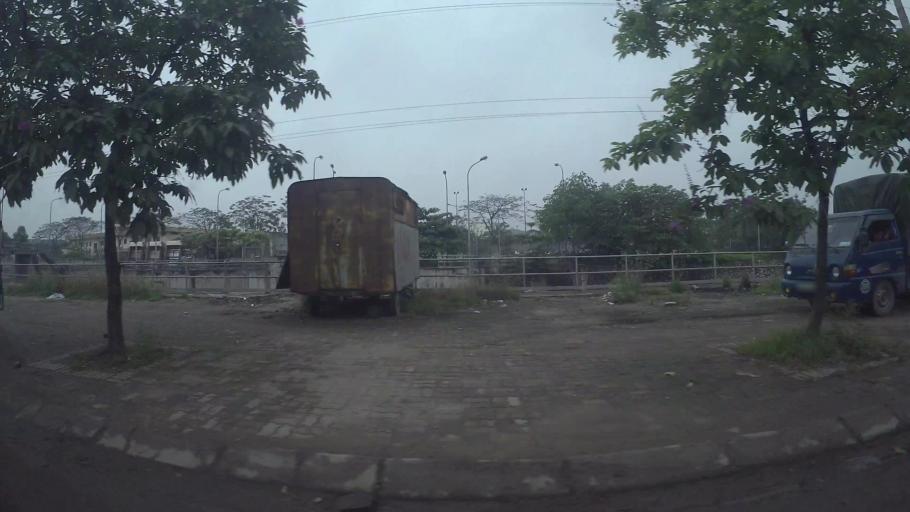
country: VN
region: Ha Noi
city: Van Dien
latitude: 20.9783
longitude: 105.8650
